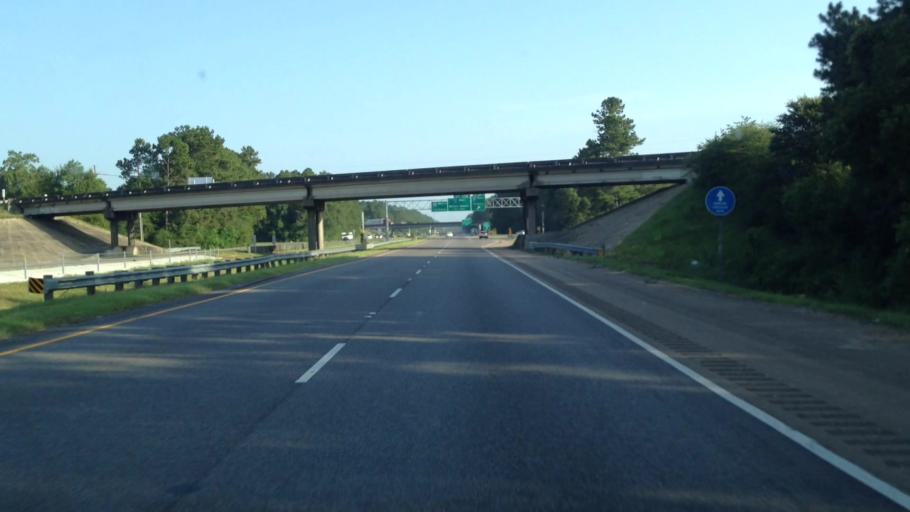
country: US
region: Louisiana
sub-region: Tangipahoa Parish
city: Hammond
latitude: 30.4748
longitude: -90.4860
